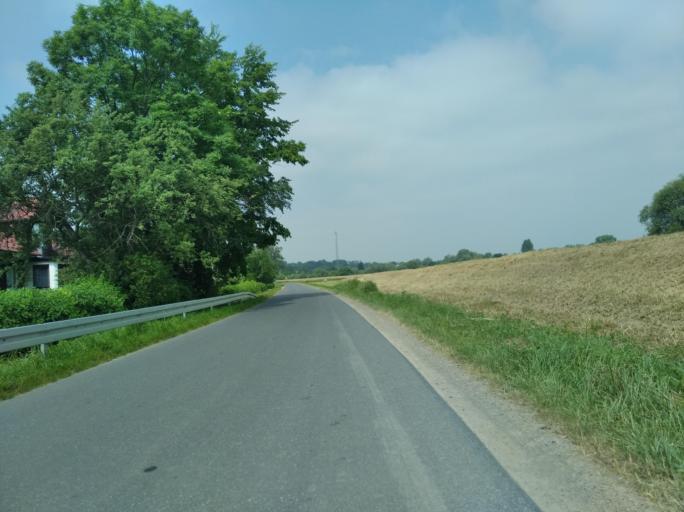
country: PL
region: Subcarpathian Voivodeship
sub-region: Powiat sanocki
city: Besko
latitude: 49.6272
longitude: 21.9311
